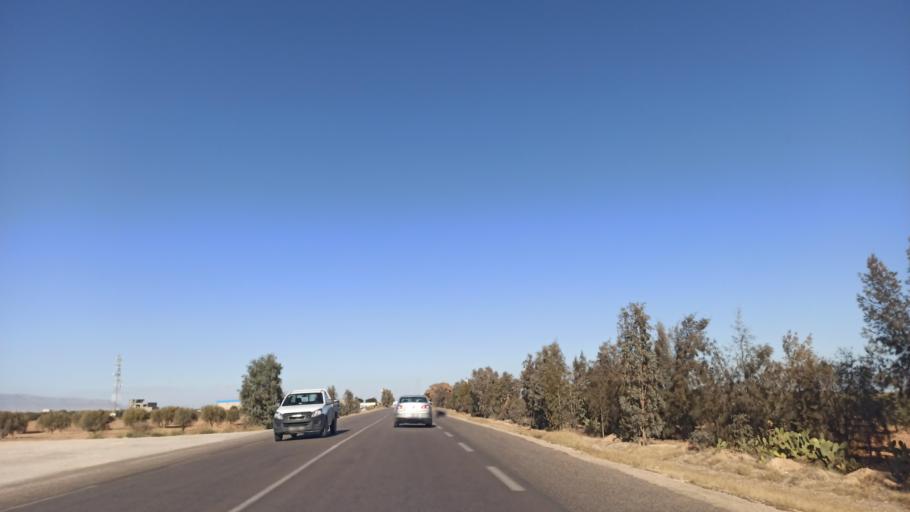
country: TN
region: Sidi Bu Zayd
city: Jilma
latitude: 35.1422
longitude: 9.3619
